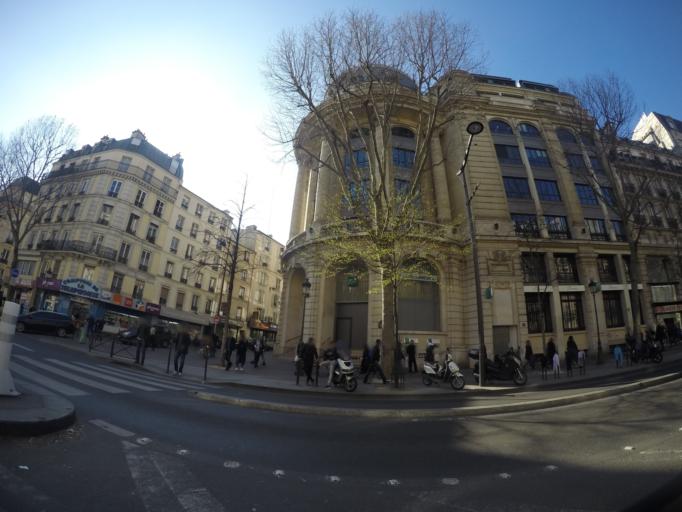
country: FR
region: Ile-de-France
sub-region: Paris
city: Saint-Ouen
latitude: 48.8845
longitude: 2.3495
